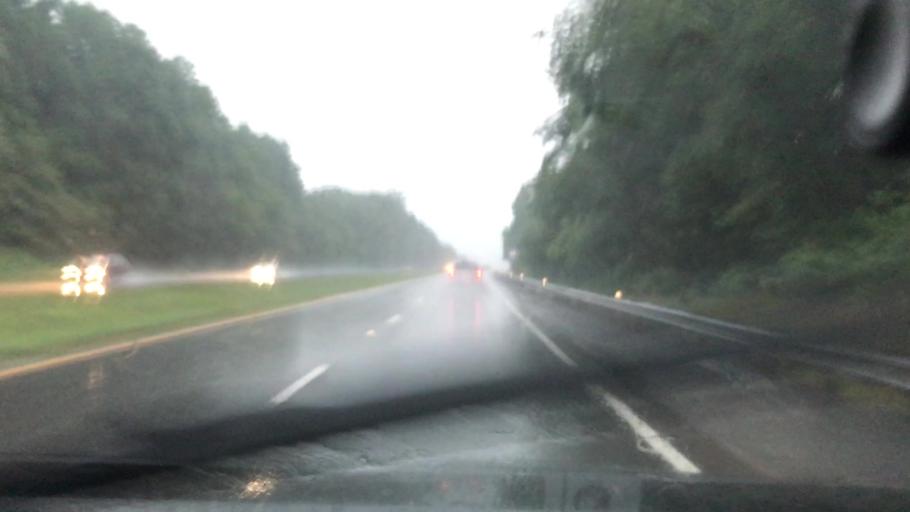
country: US
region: Virginia
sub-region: Giles County
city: Pearisburg
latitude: 37.3380
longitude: -80.7121
